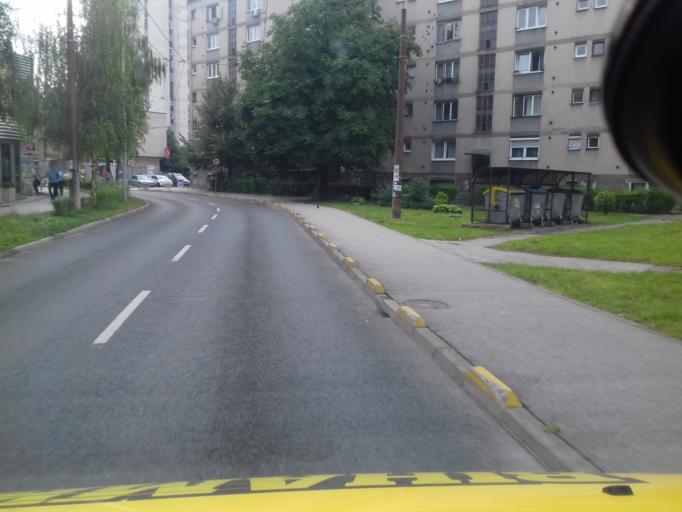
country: BA
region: Federation of Bosnia and Herzegovina
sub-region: Kanton Sarajevo
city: Sarajevo
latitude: 43.8480
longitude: 18.3690
